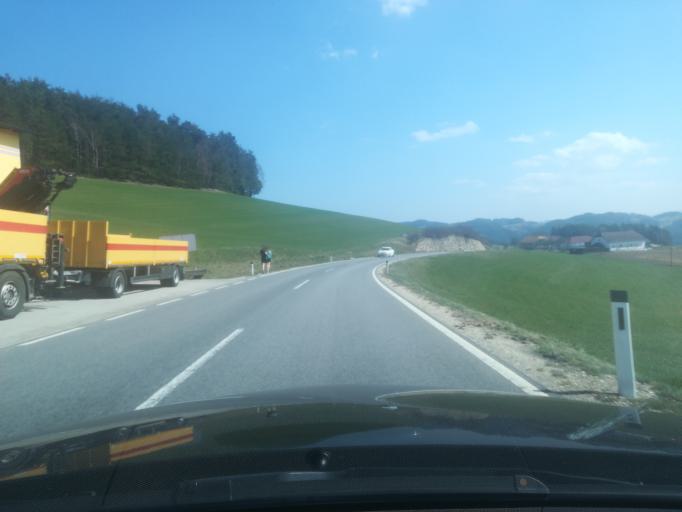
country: AT
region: Upper Austria
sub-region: Politischer Bezirk Perg
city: Bad Kreuzen
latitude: 48.4166
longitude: 14.7406
